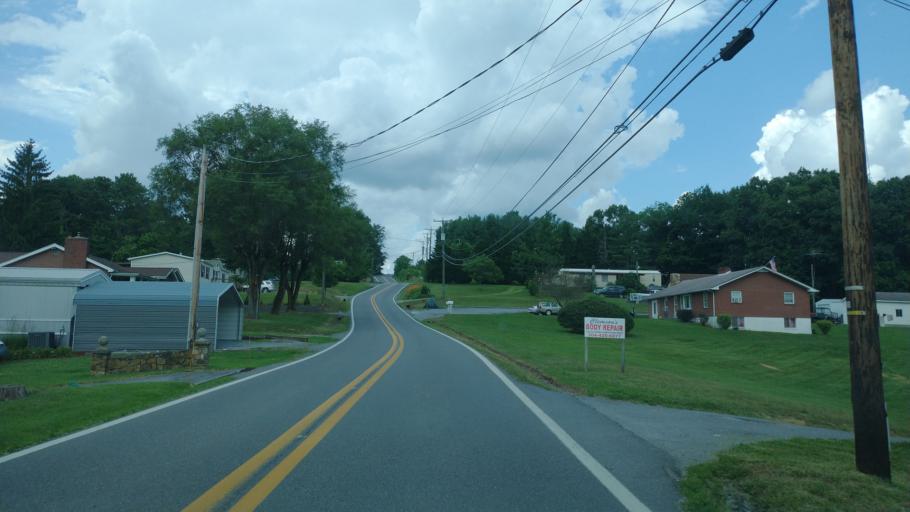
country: US
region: West Virginia
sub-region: Mercer County
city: Athens
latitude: 37.3923
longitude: -81.0577
